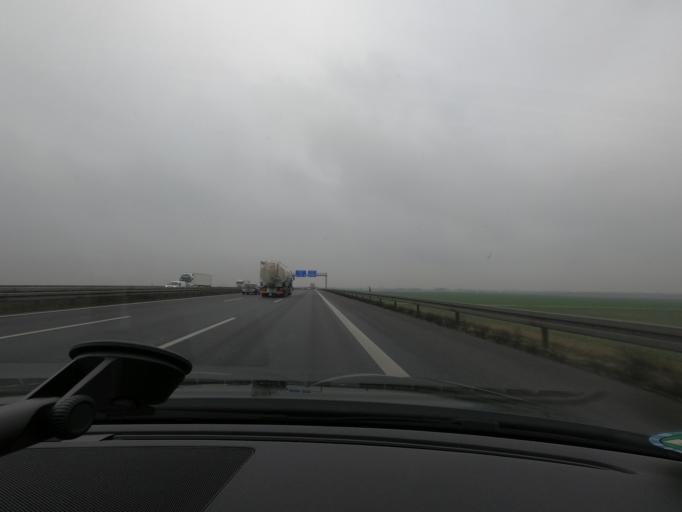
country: DE
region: North Rhine-Westphalia
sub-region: Regierungsbezirk Dusseldorf
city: Juchen
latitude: 51.0768
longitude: 6.4821
